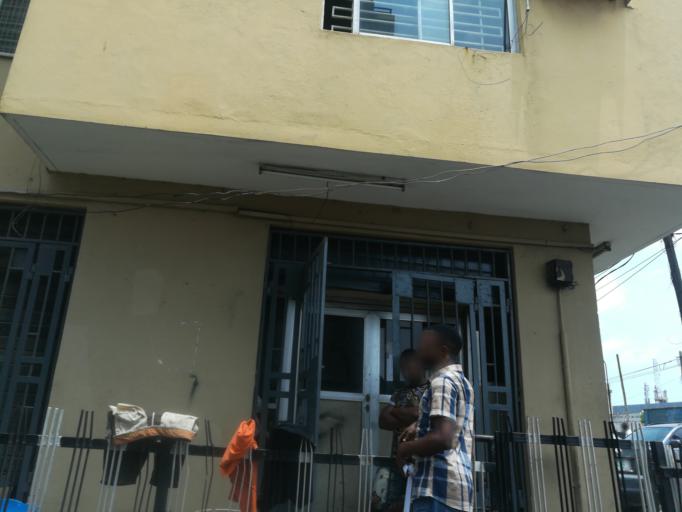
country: NG
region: Lagos
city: Lagos
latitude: 6.4506
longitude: 3.3998
